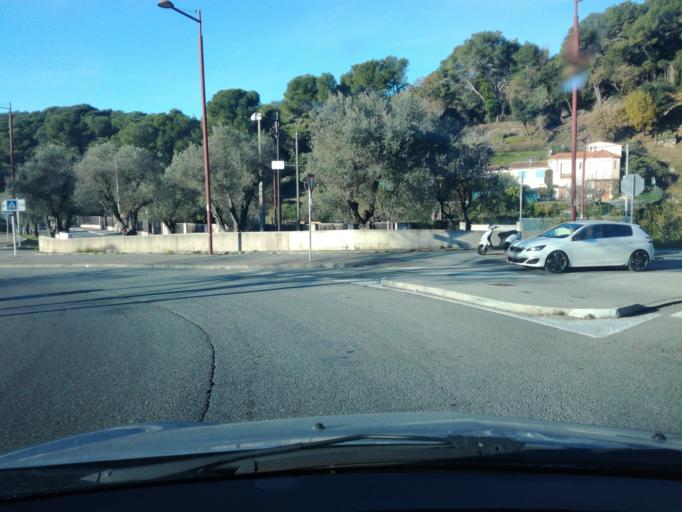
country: FR
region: Provence-Alpes-Cote d'Azur
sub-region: Departement des Alpes-Maritimes
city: Vallauris
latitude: 43.5860
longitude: 7.0910
